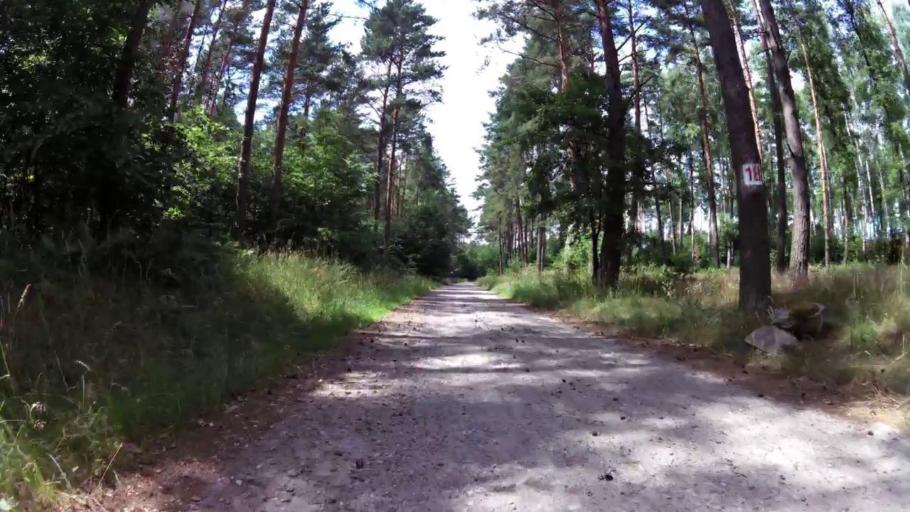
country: PL
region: West Pomeranian Voivodeship
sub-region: Powiat lobeski
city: Lobez
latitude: 53.5643
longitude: 15.6596
